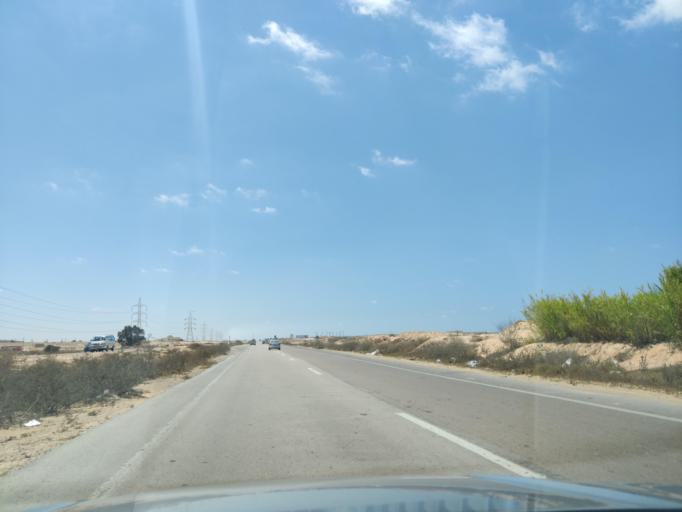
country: EG
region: Muhafazat Matruh
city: Al `Alamayn
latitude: 31.0666
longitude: 28.1802
